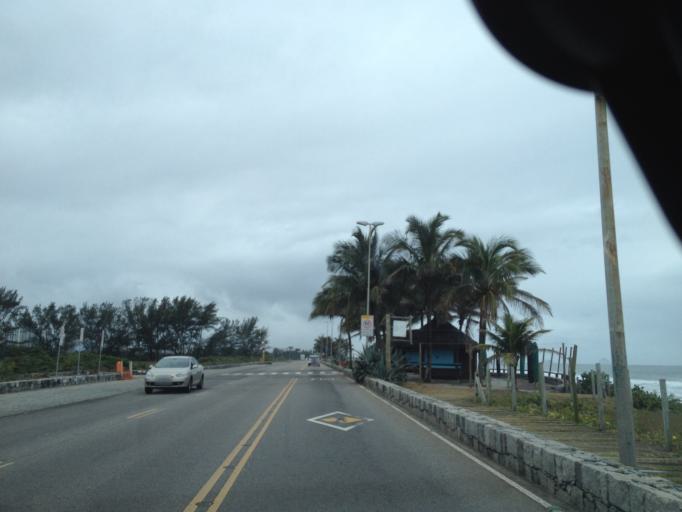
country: BR
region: Rio de Janeiro
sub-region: Nilopolis
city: Nilopolis
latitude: -23.0202
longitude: -43.4376
